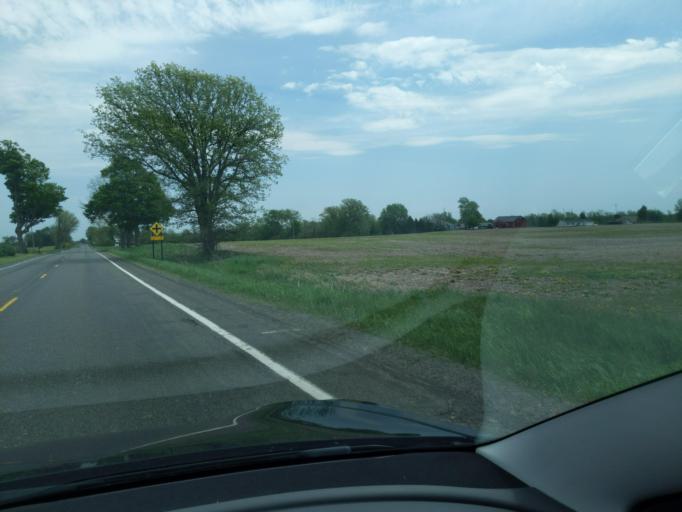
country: US
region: Michigan
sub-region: Ingham County
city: Mason
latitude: 42.5241
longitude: -84.4652
